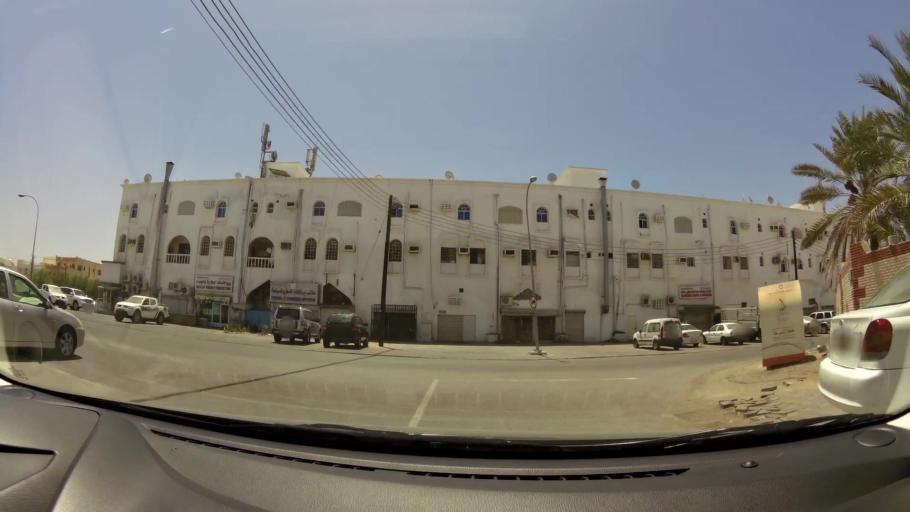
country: OM
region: Muhafazat Masqat
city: Bawshar
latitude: 23.5954
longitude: 58.3800
